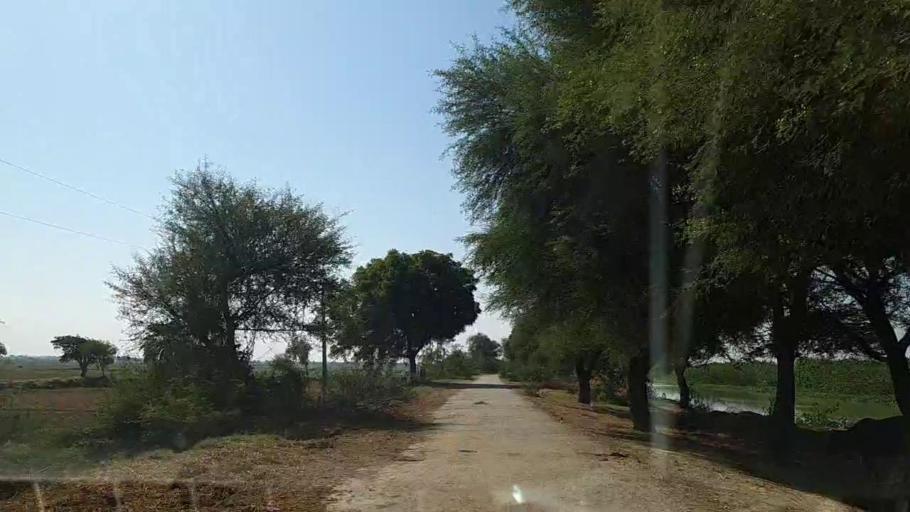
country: PK
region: Sindh
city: Chuhar Jamali
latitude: 24.5825
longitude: 68.0474
